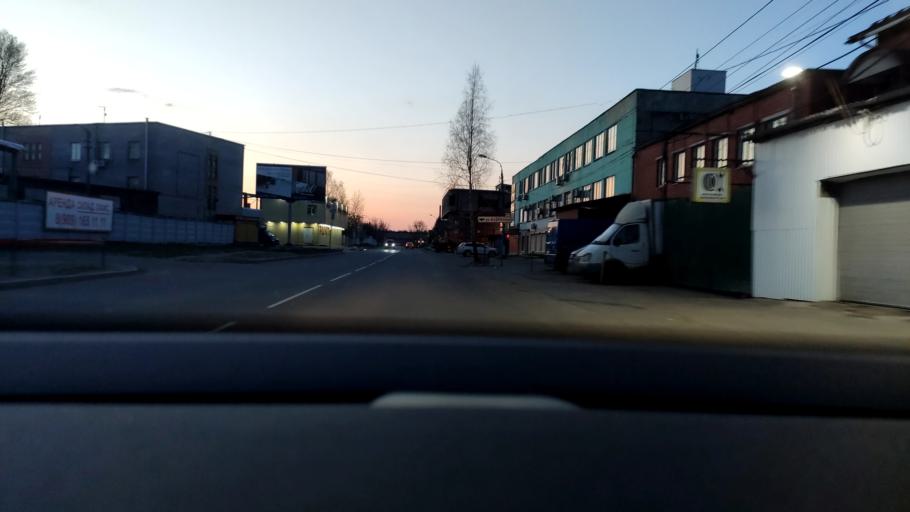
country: RU
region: Moskovskaya
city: Reutov
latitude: 55.7674
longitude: 37.8809
